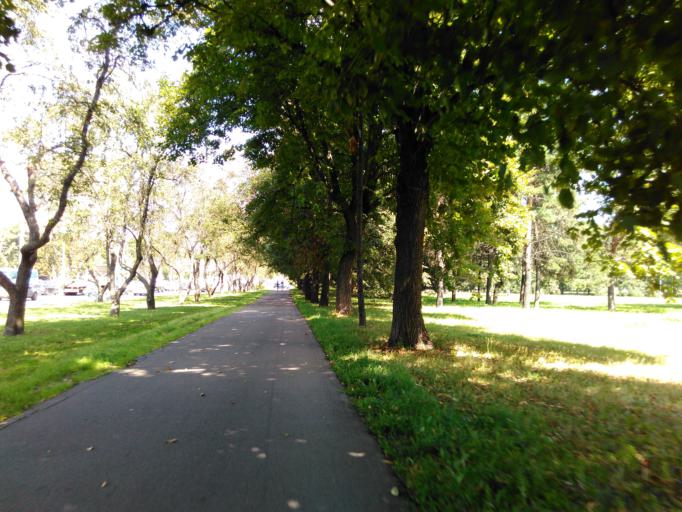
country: RU
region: Moskovskaya
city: Semenovskoye
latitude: 55.6991
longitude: 37.5447
